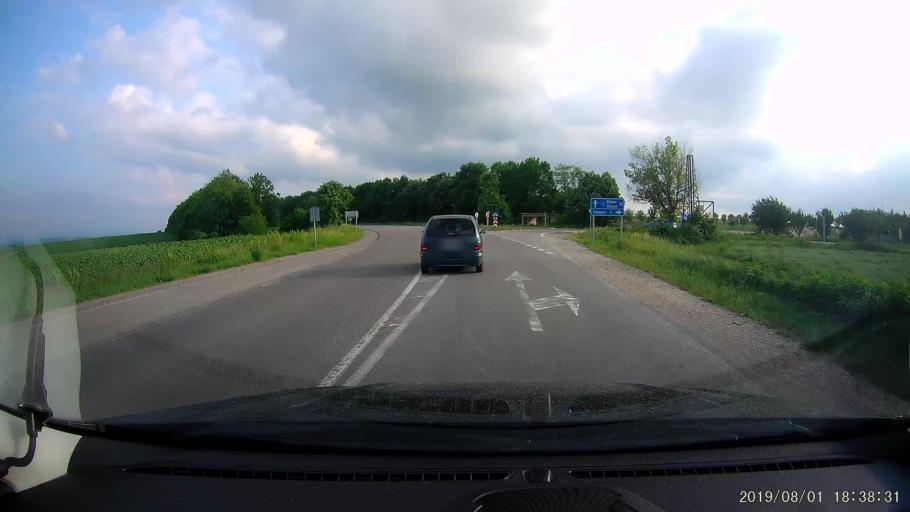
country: BG
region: Shumen
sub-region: Obshtina Khitrino
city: Gara Khitrino
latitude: 43.4008
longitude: 26.9161
